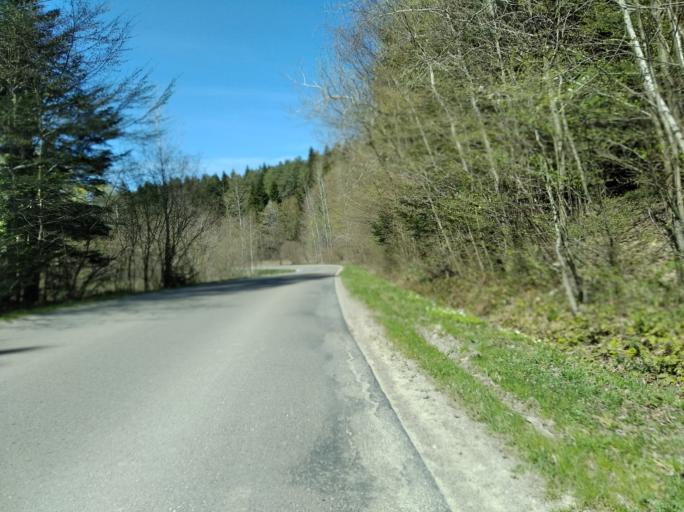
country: PL
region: Subcarpathian Voivodeship
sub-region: Powiat brzozowski
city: Golcowa
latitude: 49.7475
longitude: 22.0743
